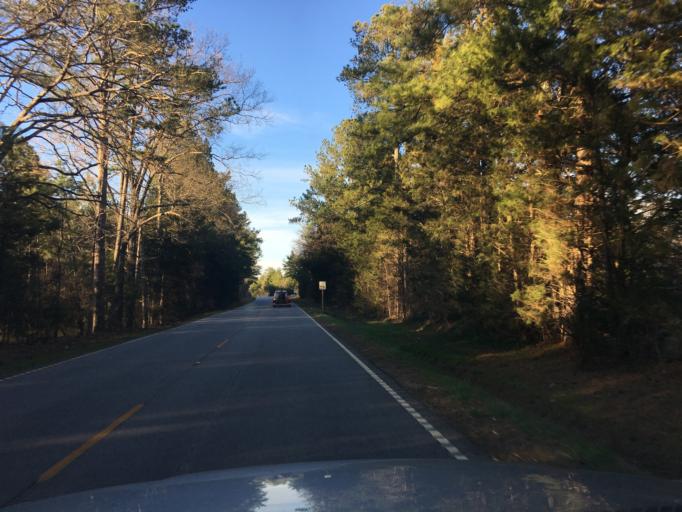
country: US
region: South Carolina
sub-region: Saluda County
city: Saluda
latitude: 34.0580
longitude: -81.8170
